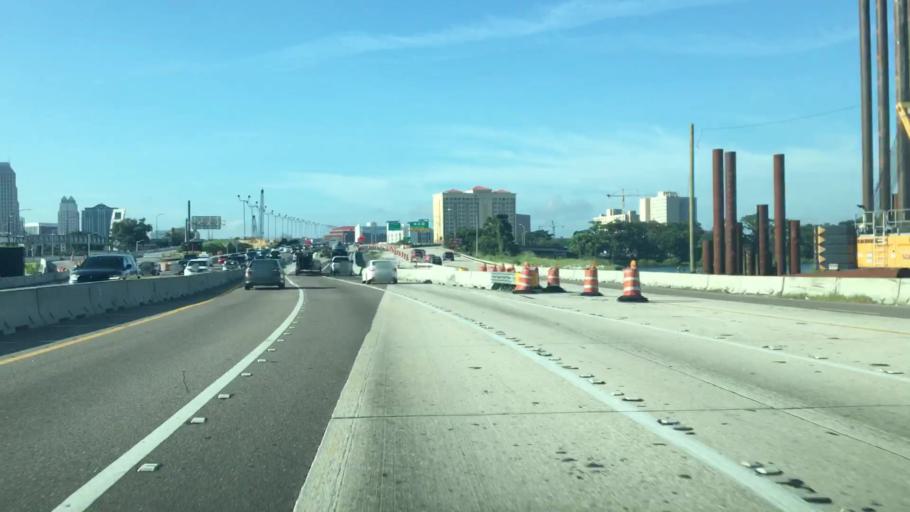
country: US
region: Florida
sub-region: Orange County
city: Orlando
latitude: 28.5569
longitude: -81.3819
